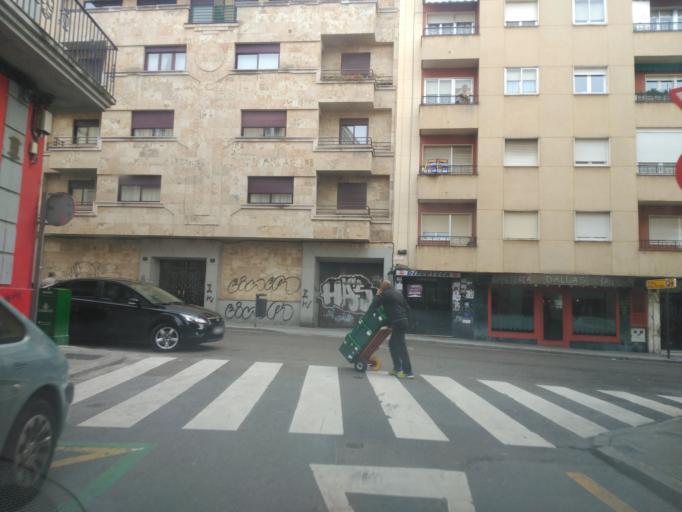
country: ES
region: Castille and Leon
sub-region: Provincia de Salamanca
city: Salamanca
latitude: 40.9726
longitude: -5.6604
